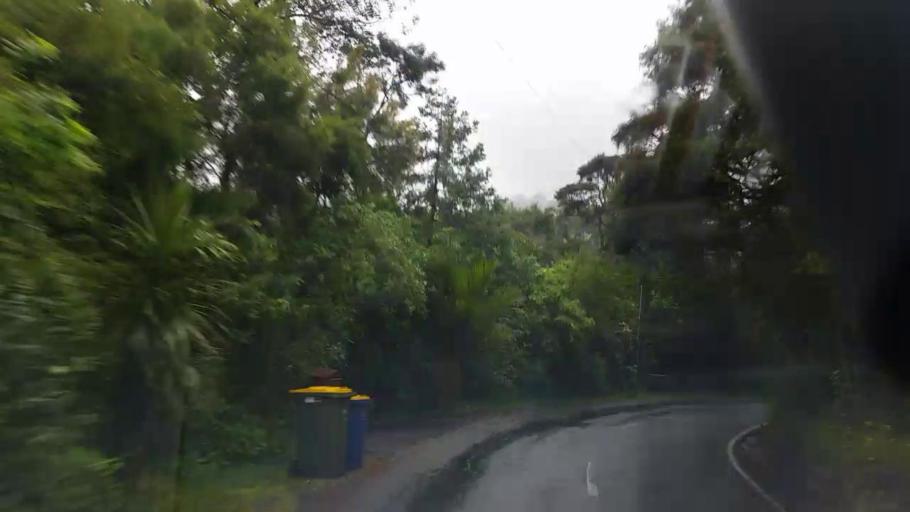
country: NZ
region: Auckland
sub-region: Auckland
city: Waitakere
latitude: -36.9037
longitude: 174.5738
